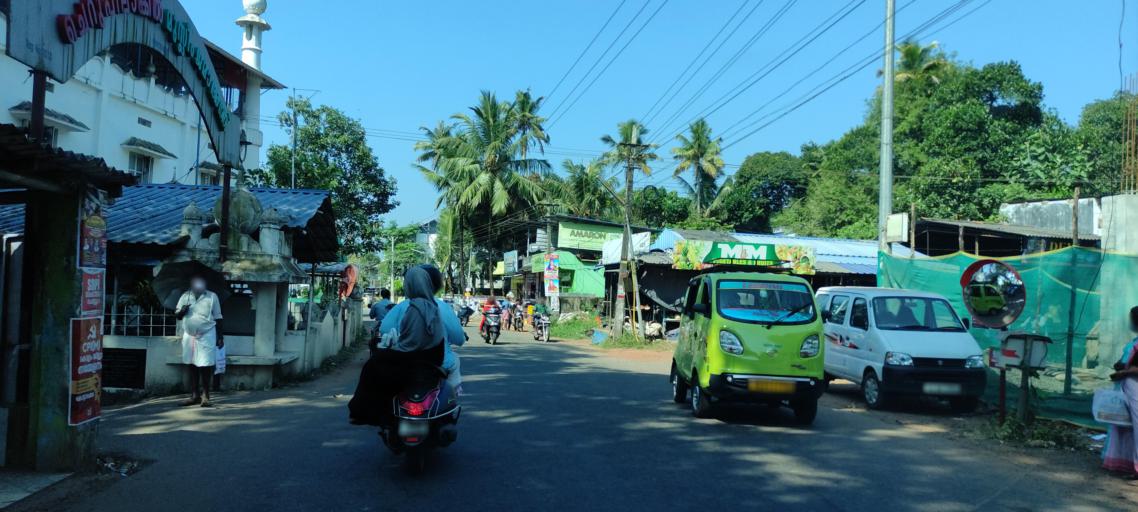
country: IN
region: Kerala
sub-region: Kollam
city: Panmana
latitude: 9.0422
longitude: 76.5876
